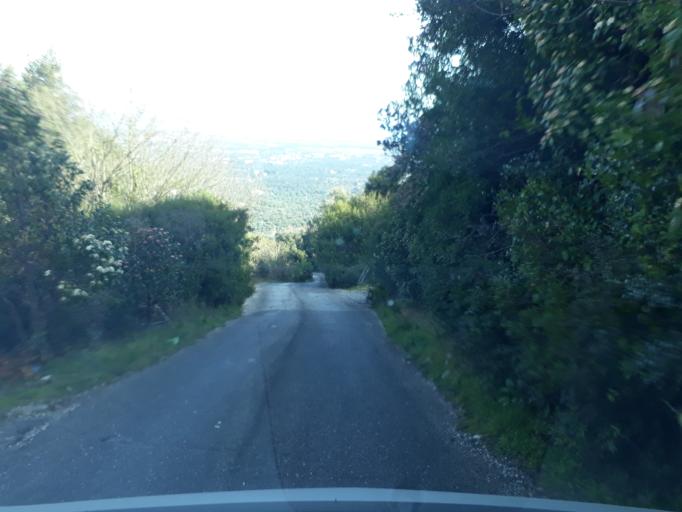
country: IT
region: Apulia
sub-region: Provincia di Brindisi
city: Lamie di Olimpie-Selva
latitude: 40.7893
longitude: 17.3682
